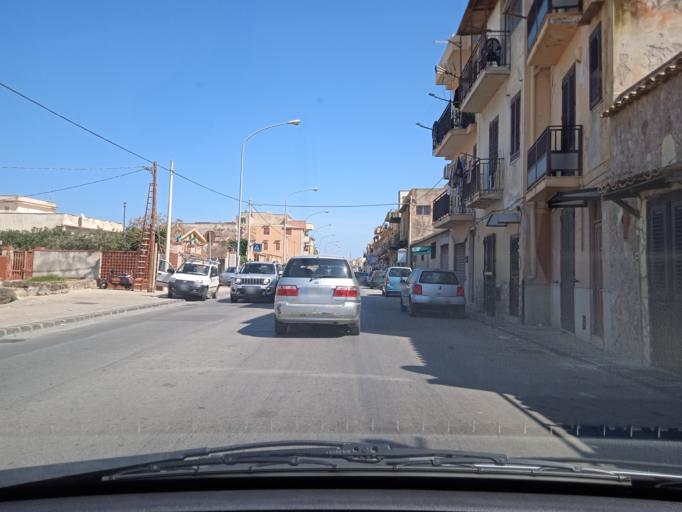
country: IT
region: Sicily
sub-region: Palermo
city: Ciaculli
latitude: 38.0984
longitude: 13.4081
